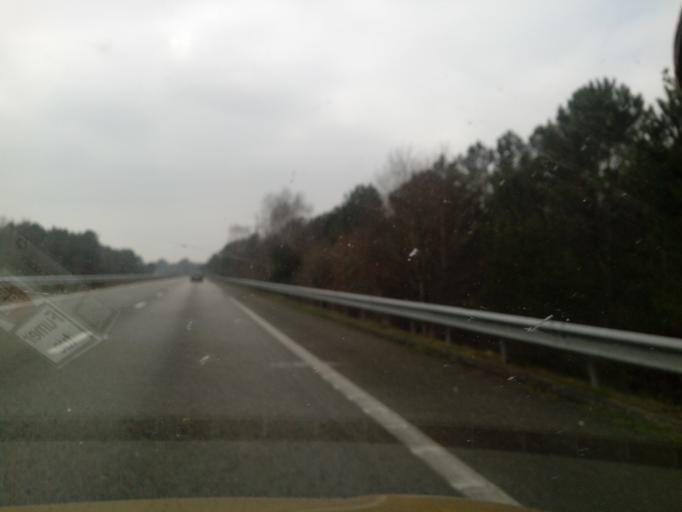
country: FR
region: Brittany
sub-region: Departement du Morbihan
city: Serent
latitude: 47.7614
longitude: -2.5294
